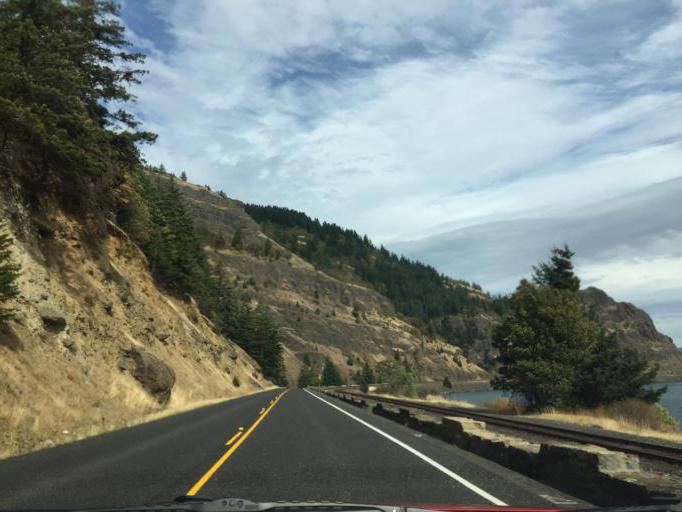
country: US
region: Washington
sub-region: Skamania County
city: Carson
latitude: 45.7081
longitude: -121.6800
